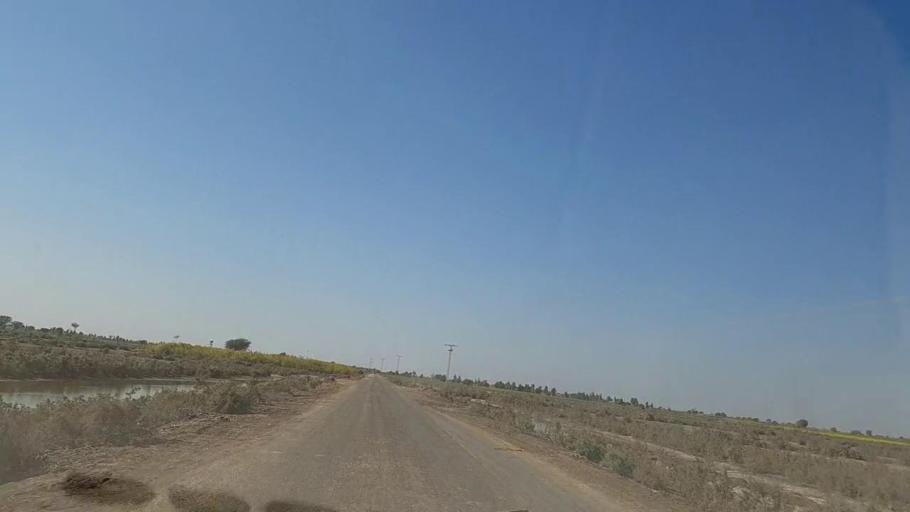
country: PK
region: Sindh
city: Digri
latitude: 25.1693
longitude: 69.0208
